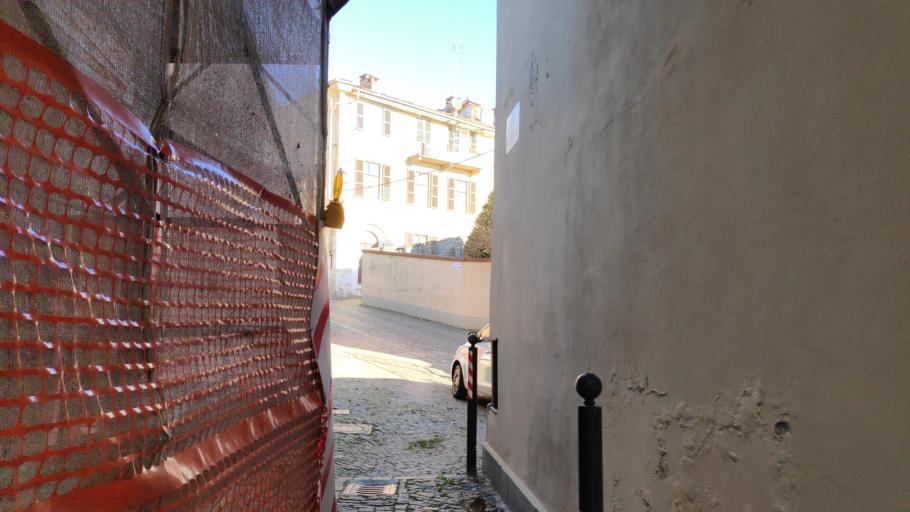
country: IT
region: Piedmont
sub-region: Provincia di Torino
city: Pinerolo
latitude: 44.8884
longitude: 7.3258
